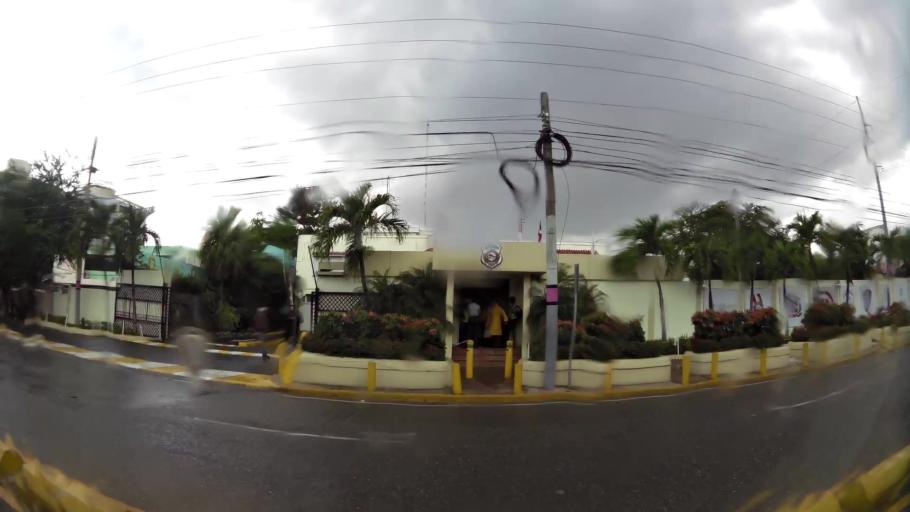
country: DO
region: Nacional
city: Ciudad Nueva
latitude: 18.4726
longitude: -69.9125
